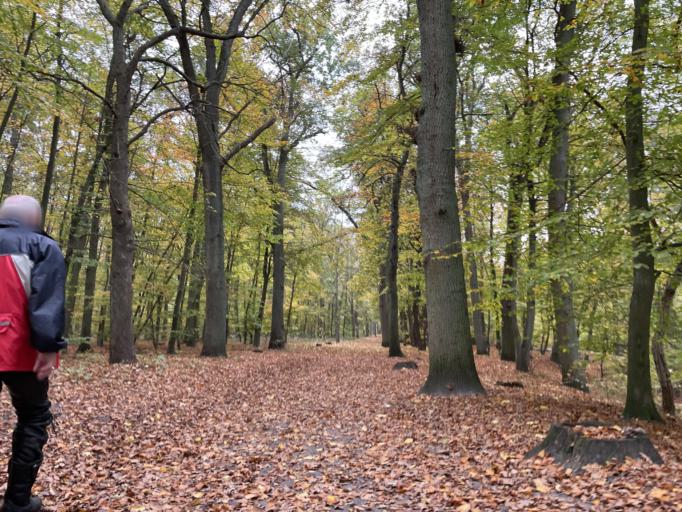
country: DE
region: Lower Saxony
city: Lueneburg
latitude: 53.2232
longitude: 10.3966
